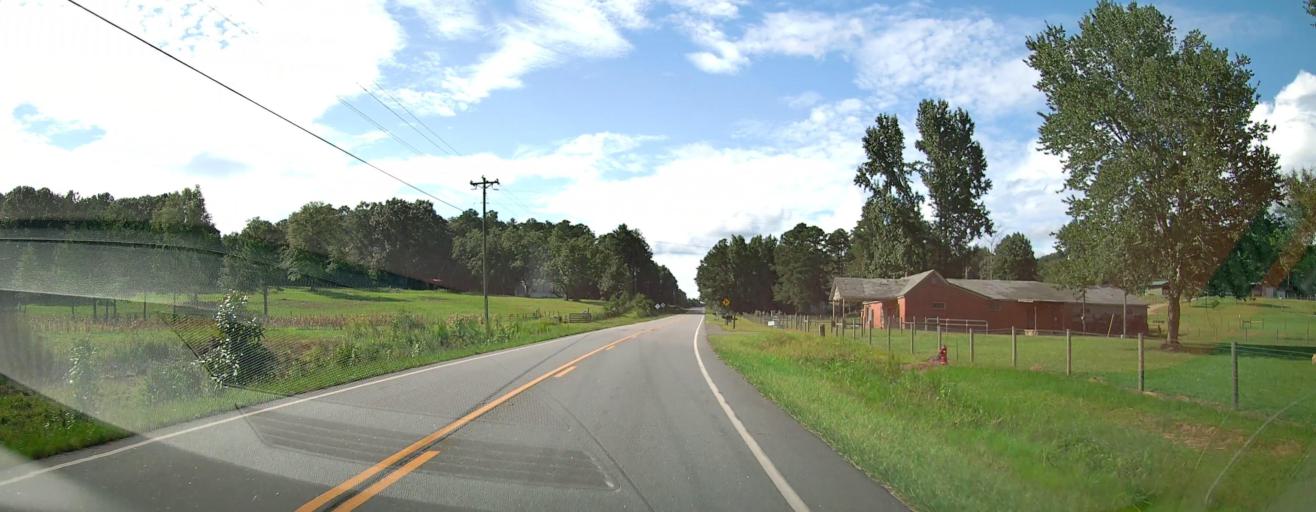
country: US
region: Georgia
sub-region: Upson County
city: Hannahs Mill
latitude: 32.9338
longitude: -84.4486
